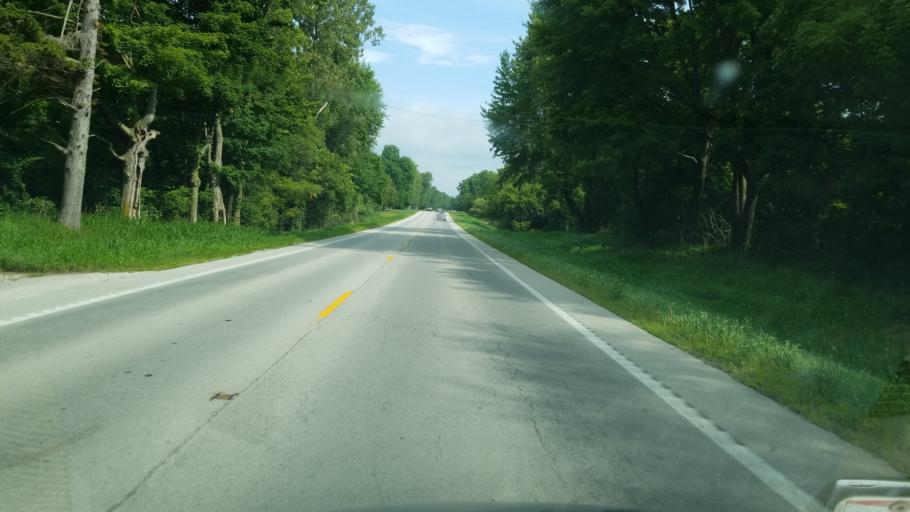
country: US
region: Ohio
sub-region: Sandusky County
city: Ballville
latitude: 41.2659
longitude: -83.1682
